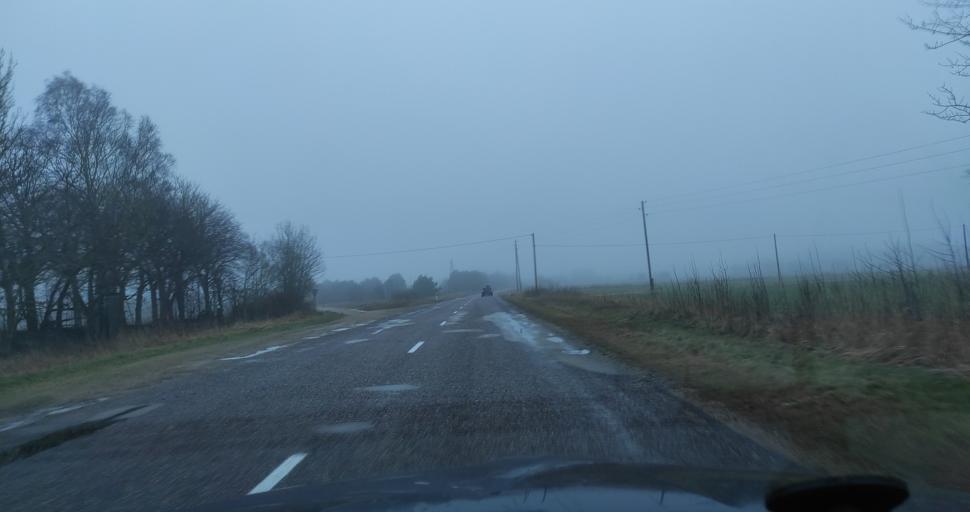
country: LV
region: Alsunga
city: Alsunga
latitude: 57.1205
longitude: 21.4248
